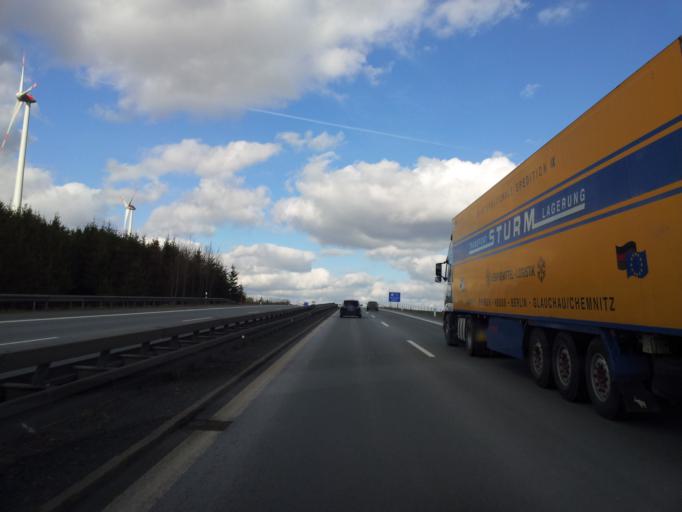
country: DE
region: Bavaria
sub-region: Upper Franconia
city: Topen
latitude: 50.3623
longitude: 11.8805
